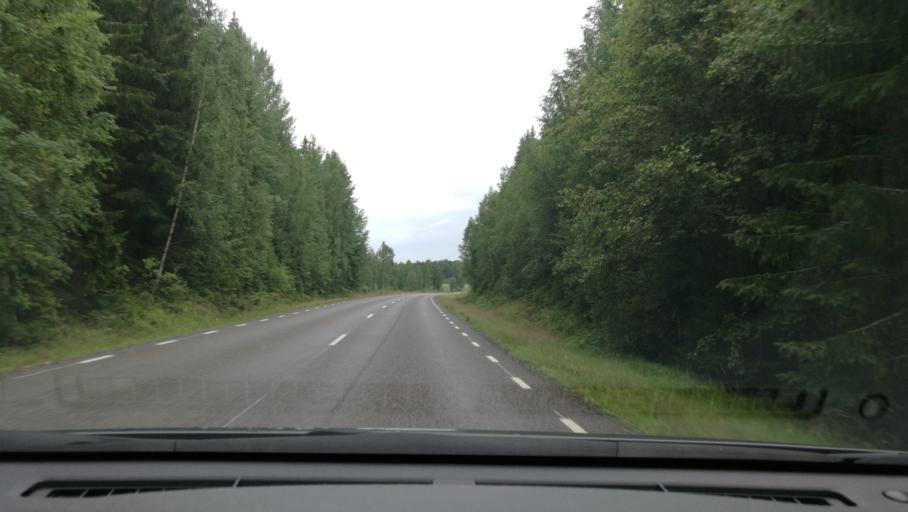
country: SE
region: OEstergoetland
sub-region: Norrkopings Kommun
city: Svartinge
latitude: 58.7830
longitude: 15.9660
